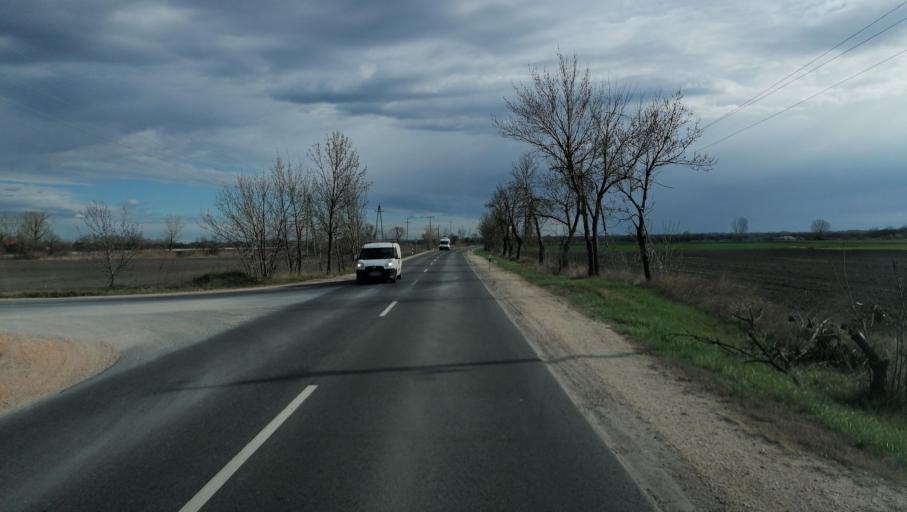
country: HU
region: Pest
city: Bugyi
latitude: 47.2403
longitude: 19.1916
